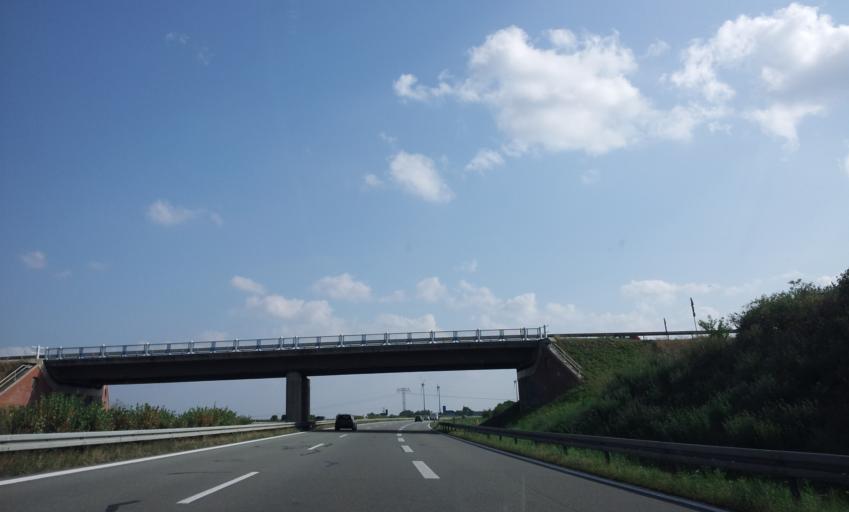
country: DE
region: Mecklenburg-Vorpommern
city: Jarmen
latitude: 53.9139
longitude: 13.3531
